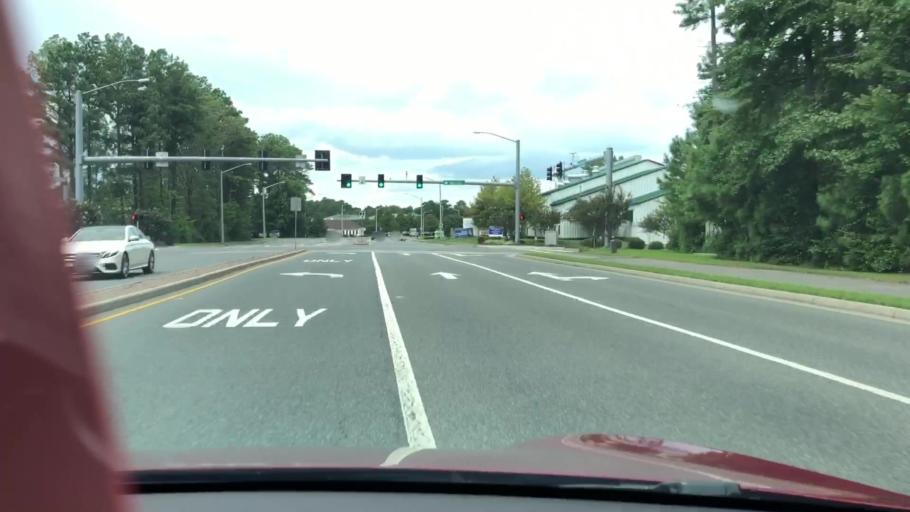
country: US
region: Virginia
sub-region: City of Virginia Beach
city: Virginia Beach
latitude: 36.8196
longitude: -75.9995
